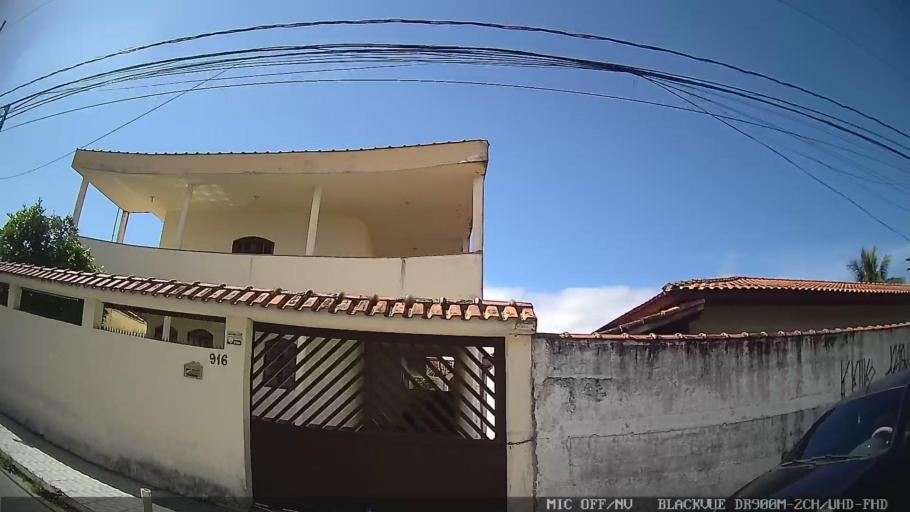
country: BR
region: Sao Paulo
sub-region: Peruibe
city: Peruibe
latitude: -24.3217
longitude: -46.9961
